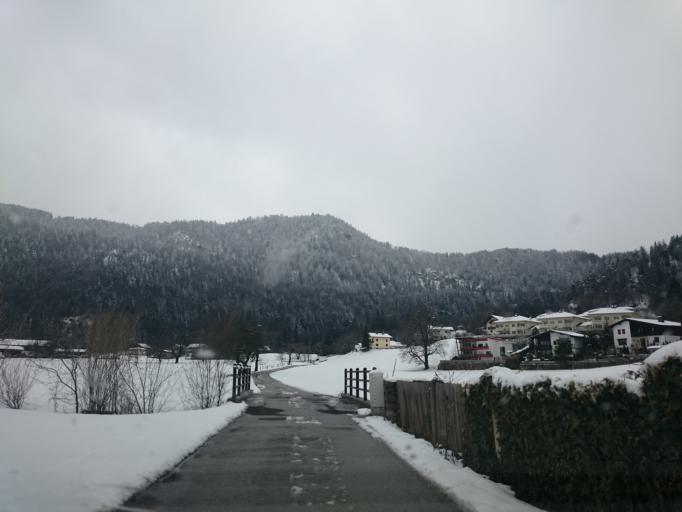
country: AT
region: Tyrol
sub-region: Politischer Bezirk Kufstein
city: Kufstein
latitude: 47.5885
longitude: 12.1589
